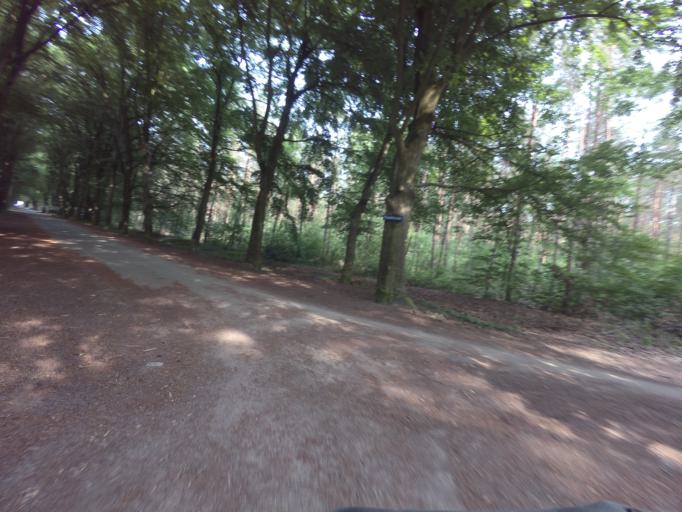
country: NL
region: North Holland
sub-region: Gemeente Hilversum
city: Hilversum
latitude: 52.1767
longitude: 5.2122
